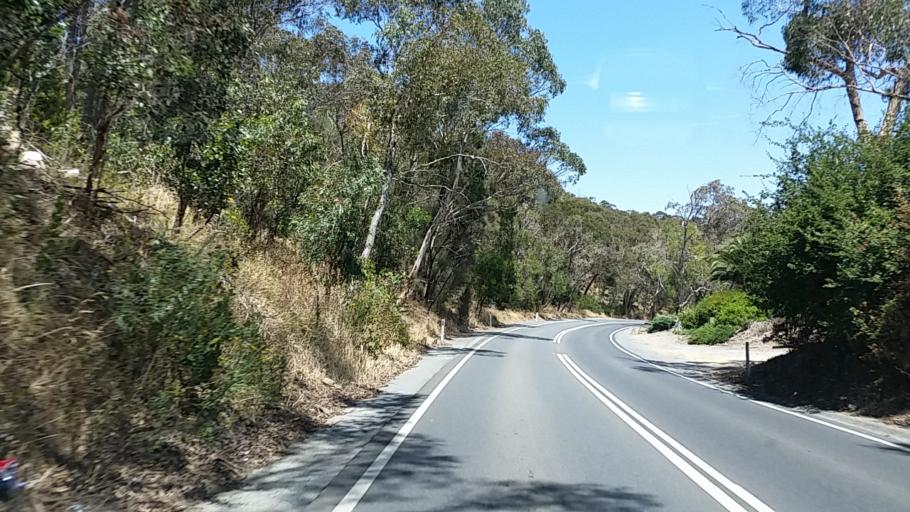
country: AU
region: South Australia
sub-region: Tea Tree Gully
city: Golden Grove
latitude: -34.8235
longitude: 138.7519
